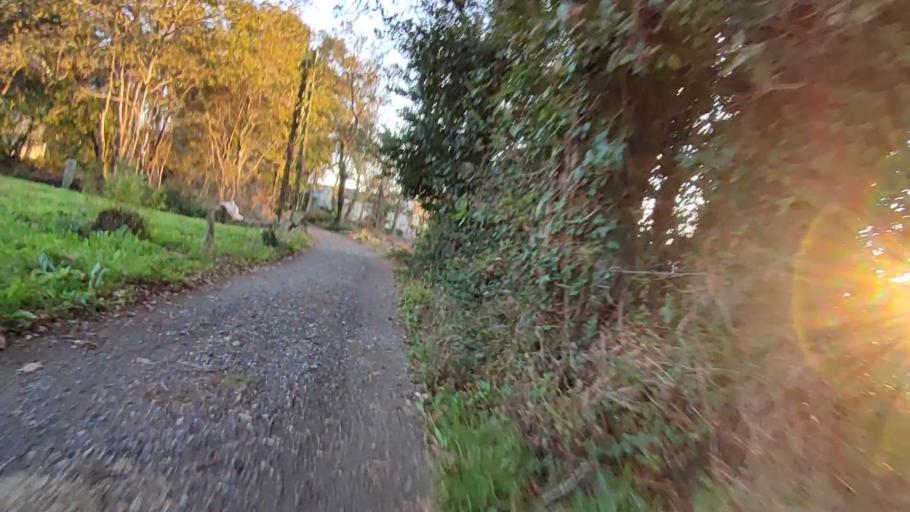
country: ES
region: Galicia
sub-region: Provincia da Coruna
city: Boiro
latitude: 42.6397
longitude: -8.8772
